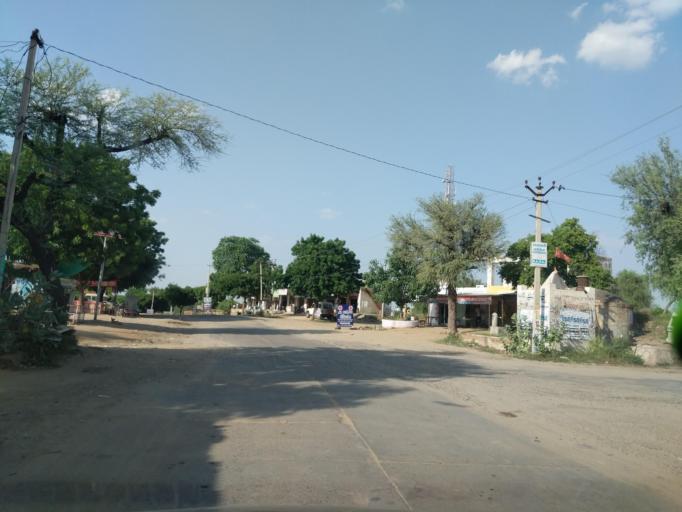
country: IN
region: Rajasthan
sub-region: Churu
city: Rajgarh
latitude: 28.5097
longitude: 75.3837
